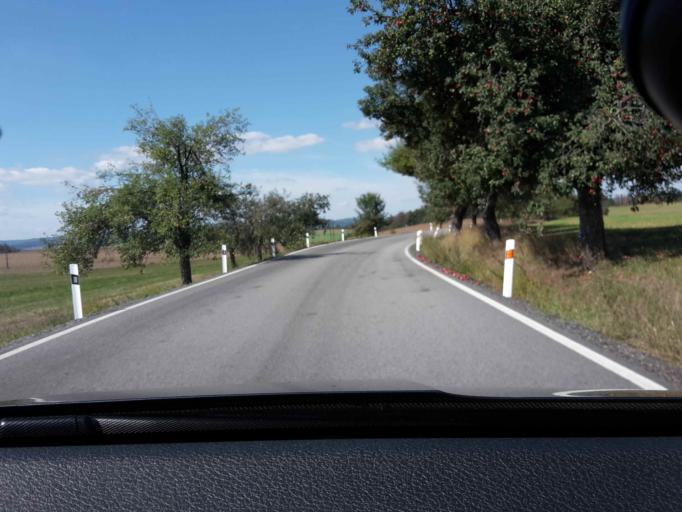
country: CZ
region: Vysocina
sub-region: Okres Jihlava
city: Telc
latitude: 49.1575
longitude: 15.5210
